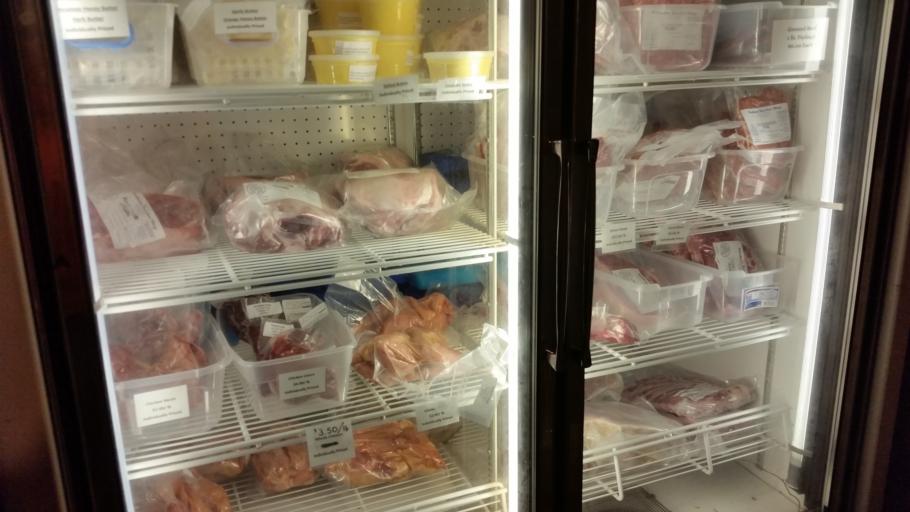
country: US
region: New Hampshire
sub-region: Carroll County
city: Ossipee
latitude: 43.6938
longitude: -71.0534
